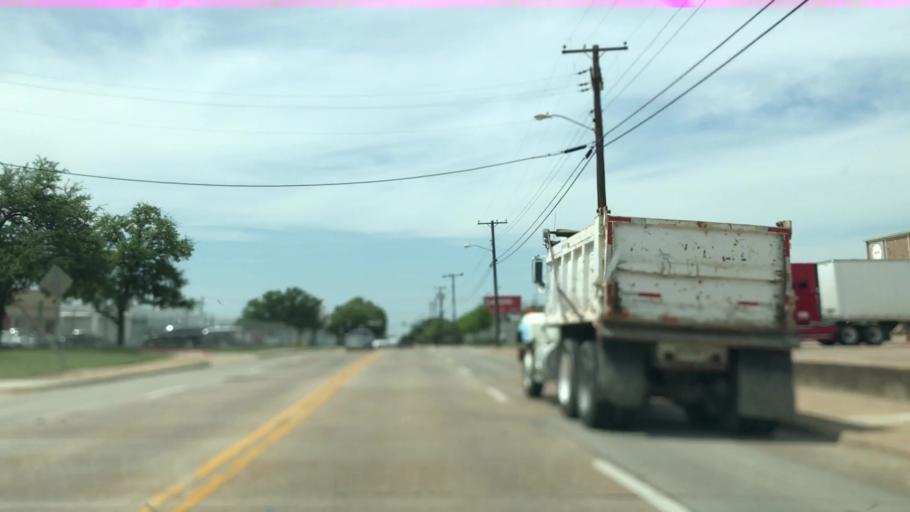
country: US
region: Texas
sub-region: Dallas County
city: University Park
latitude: 32.8289
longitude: -96.8348
